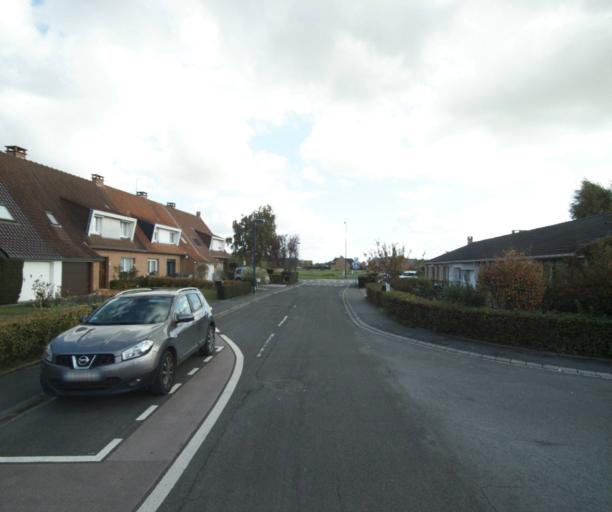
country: FR
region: Nord-Pas-de-Calais
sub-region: Departement du Nord
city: Houplines
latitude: 50.6962
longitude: 2.9203
